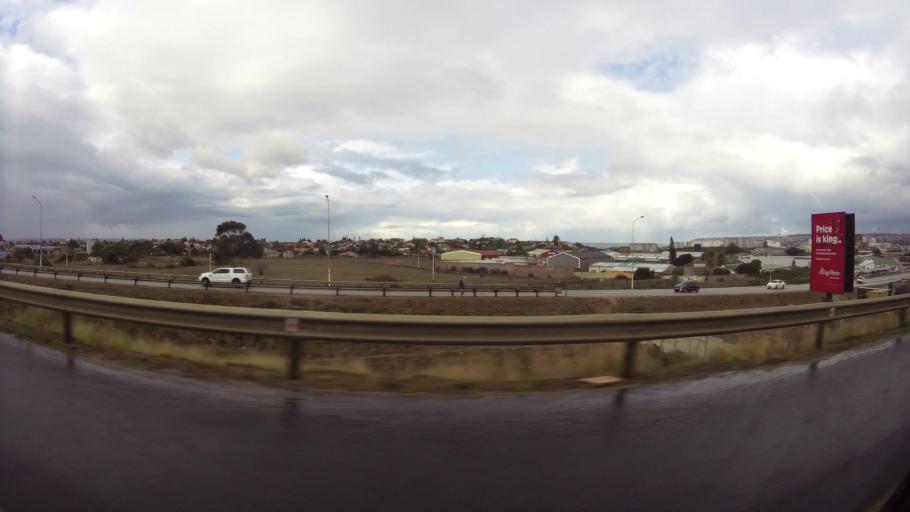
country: ZA
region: Western Cape
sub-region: Eden District Municipality
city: Mossel Bay
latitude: -34.1393
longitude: 22.1007
